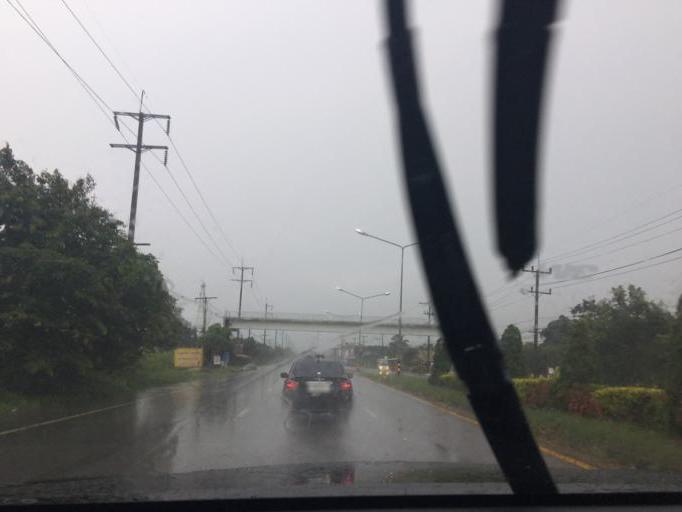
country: TH
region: Chiang Rai
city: Mae Fa Luang
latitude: 20.2315
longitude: 99.8562
